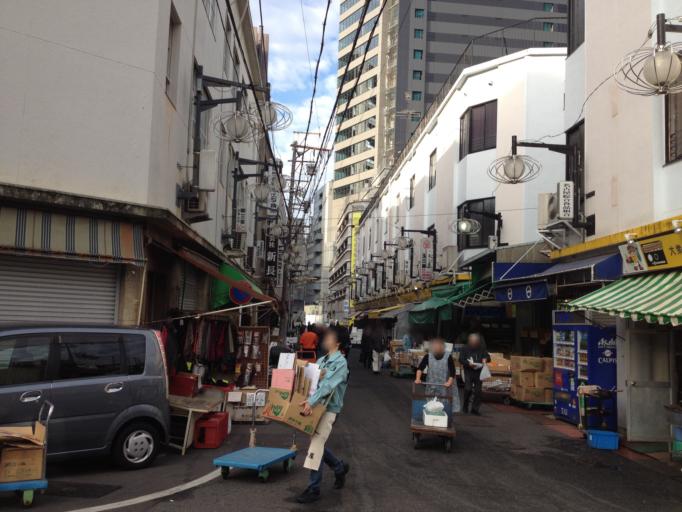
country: JP
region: Aichi
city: Nagoya-shi
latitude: 35.1697
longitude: 136.8885
